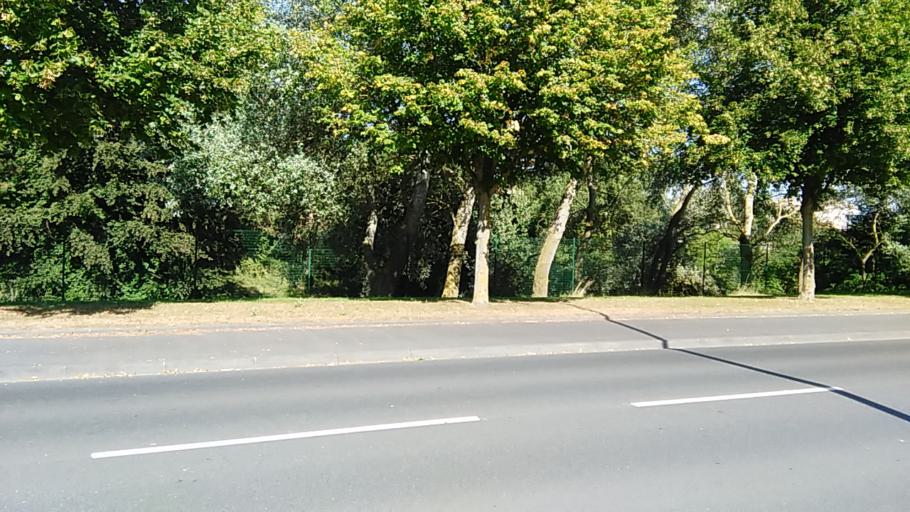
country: FR
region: Lower Normandy
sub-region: Departement du Calvados
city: Saint-Contest
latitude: 49.1978
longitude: -0.3883
